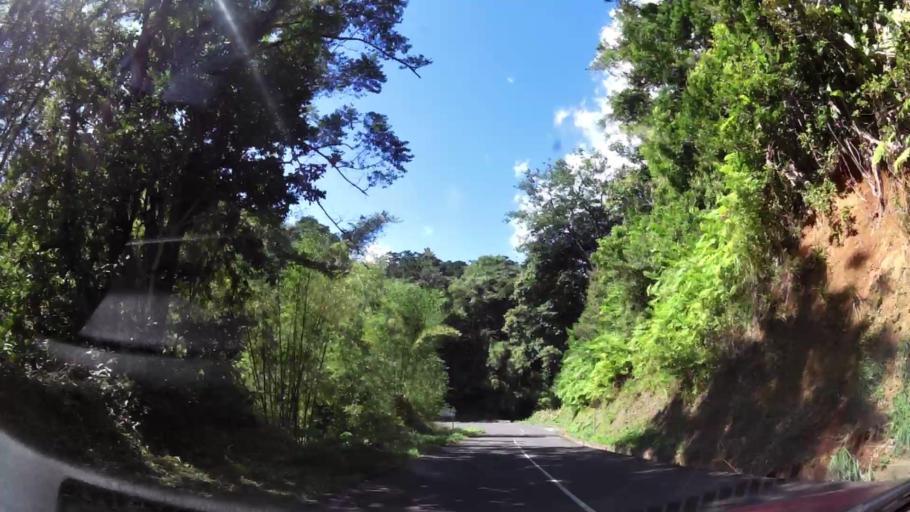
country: DM
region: Saint Paul
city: Pont Casse
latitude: 15.3523
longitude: -61.3614
